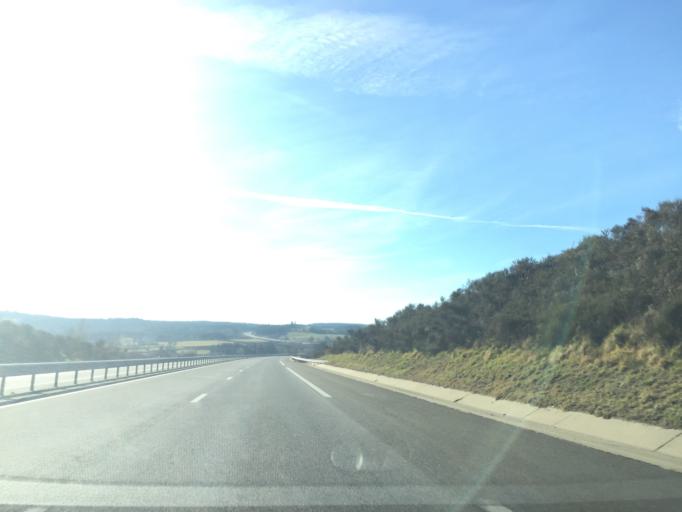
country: FR
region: Auvergne
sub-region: Departement du Puy-de-Dome
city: Gelles
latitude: 45.7798
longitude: 2.7422
